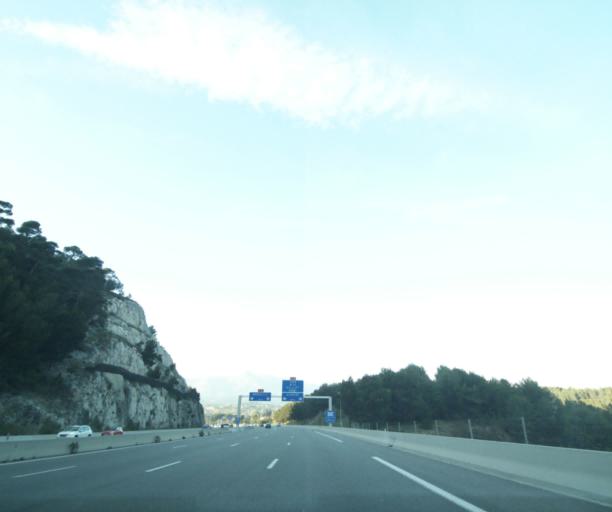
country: FR
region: Provence-Alpes-Cote d'Azur
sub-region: Departement des Bouches-du-Rhone
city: Aubagne
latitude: 43.2746
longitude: 5.5887
